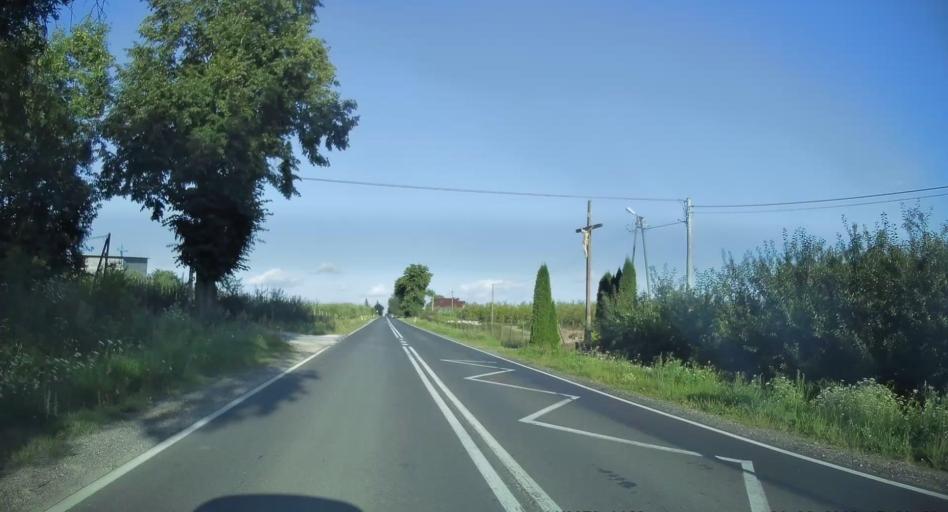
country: PL
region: Masovian Voivodeship
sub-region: Powiat grojecki
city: Bledow
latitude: 51.8038
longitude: 20.5944
